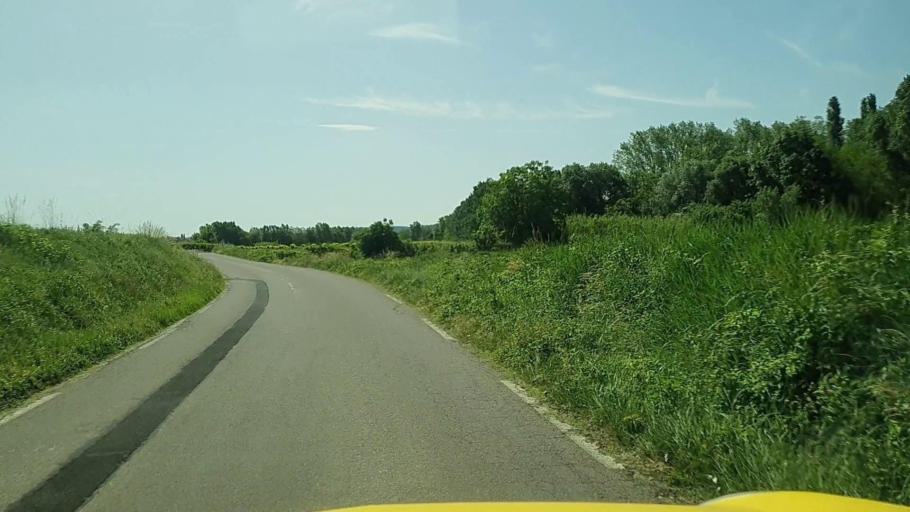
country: FR
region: Languedoc-Roussillon
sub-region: Departement du Gard
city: Sabran
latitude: 44.1057
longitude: 4.5392
